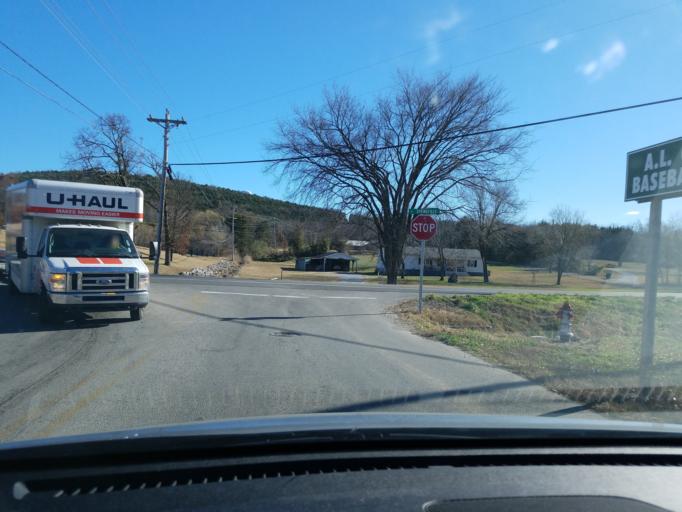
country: US
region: Arkansas
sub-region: Carroll County
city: Berryville
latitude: 36.3816
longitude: -93.5676
